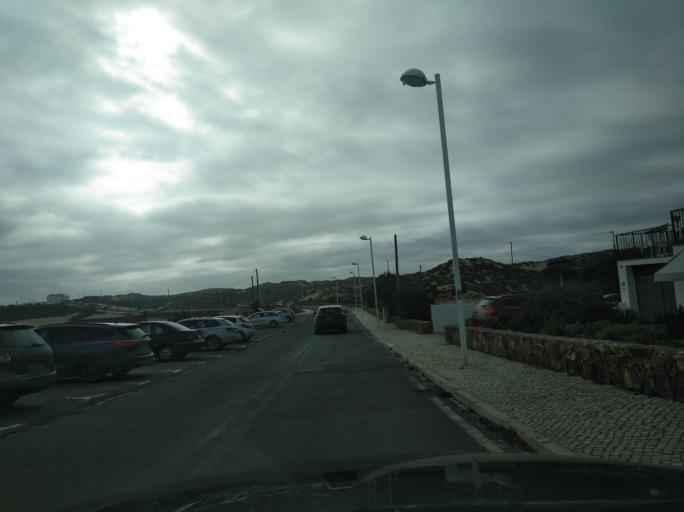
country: PT
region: Beja
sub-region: Odemira
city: Vila Nova de Milfontes
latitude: 37.7231
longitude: -8.7868
